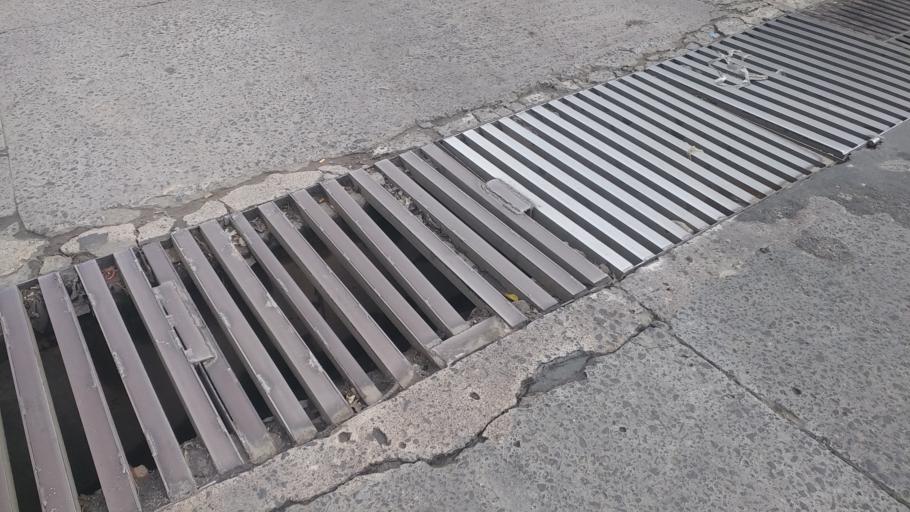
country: MX
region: Veracruz
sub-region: Xalapa
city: Xalapa de Enriquez
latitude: 19.5364
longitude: -96.9192
